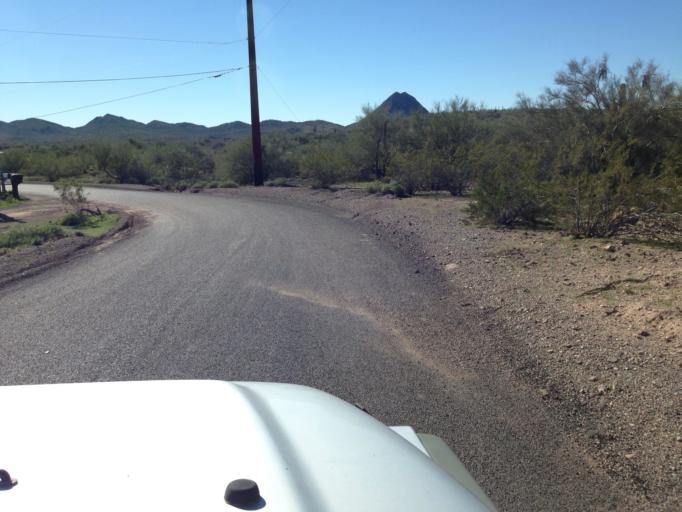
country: US
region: Arizona
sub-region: Maricopa County
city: New River
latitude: 33.9262
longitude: -112.0911
